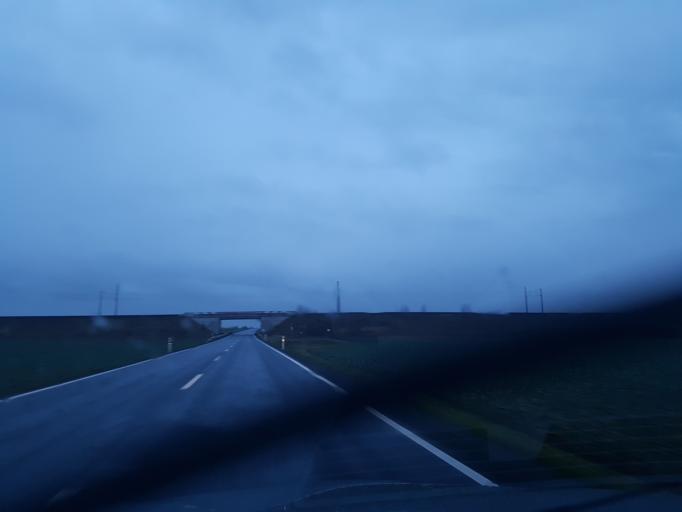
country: DE
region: Saxony
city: Priestewitz
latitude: 51.2684
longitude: 13.5167
